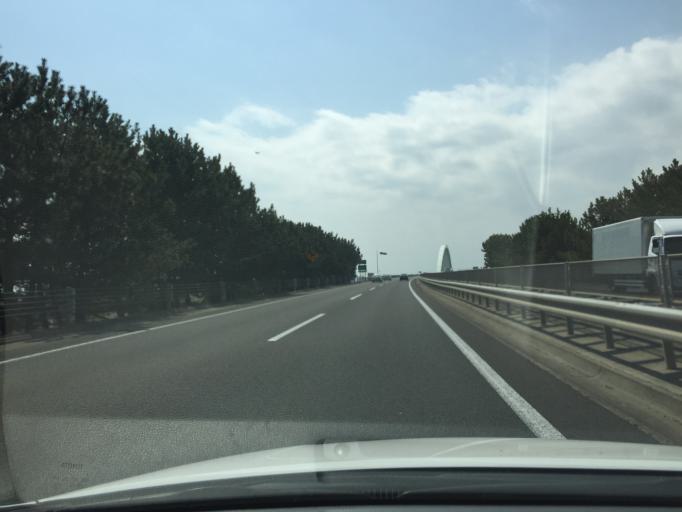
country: JP
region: Miyagi
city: Sendai
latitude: 38.1937
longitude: 140.9403
